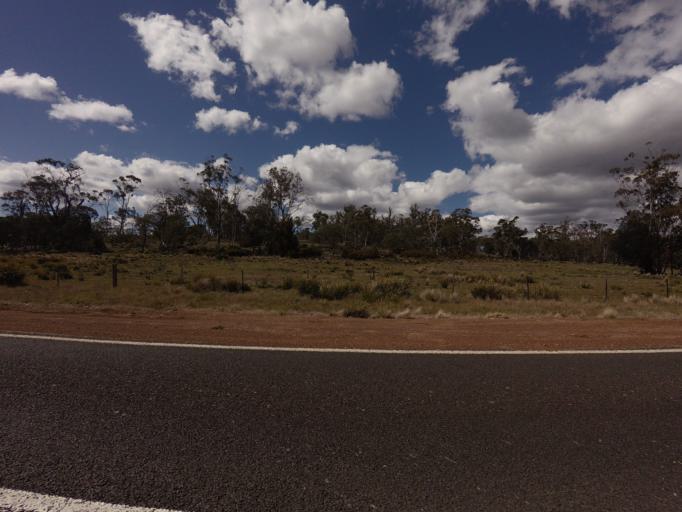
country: AU
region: Tasmania
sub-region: Northern Midlands
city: Evandale
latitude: -41.9515
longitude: 147.6093
